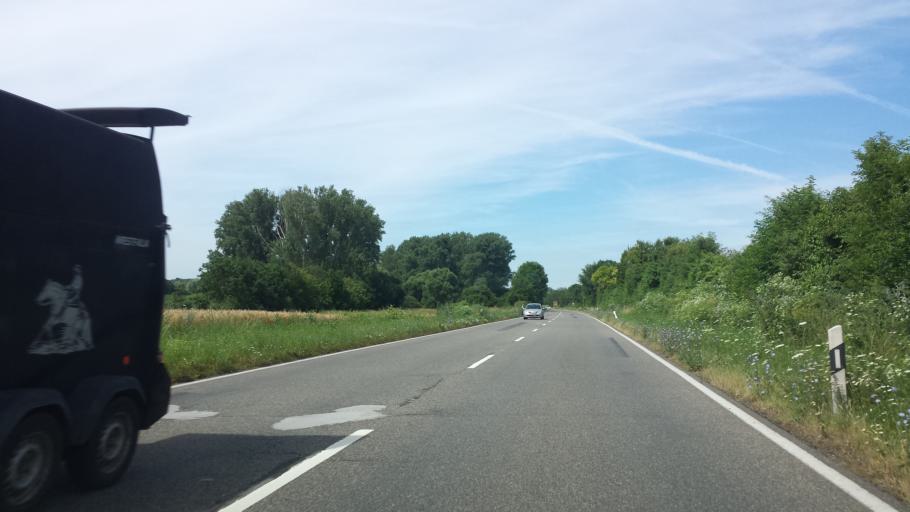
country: DE
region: Rheinland-Pfalz
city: Osthofen
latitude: 49.6753
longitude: 8.3122
